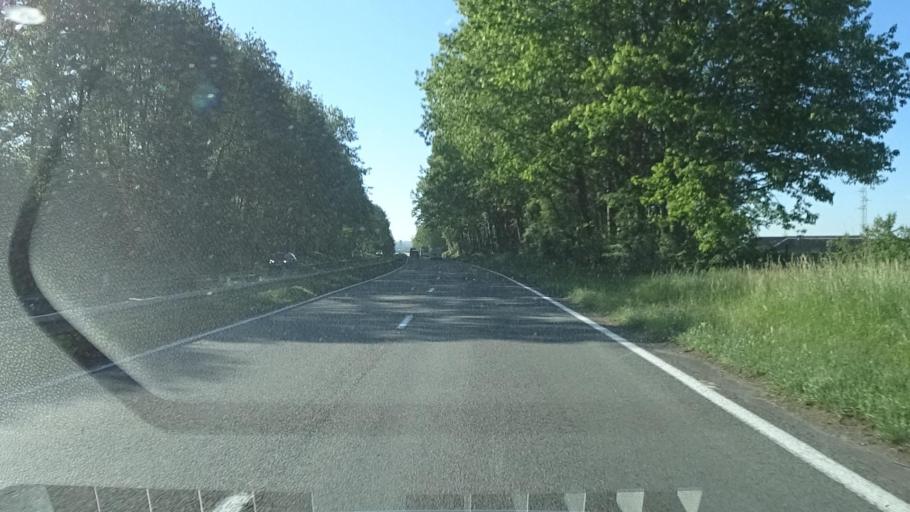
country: BE
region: Wallonia
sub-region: Province du Hainaut
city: Roeulx
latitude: 50.4627
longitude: 4.1416
